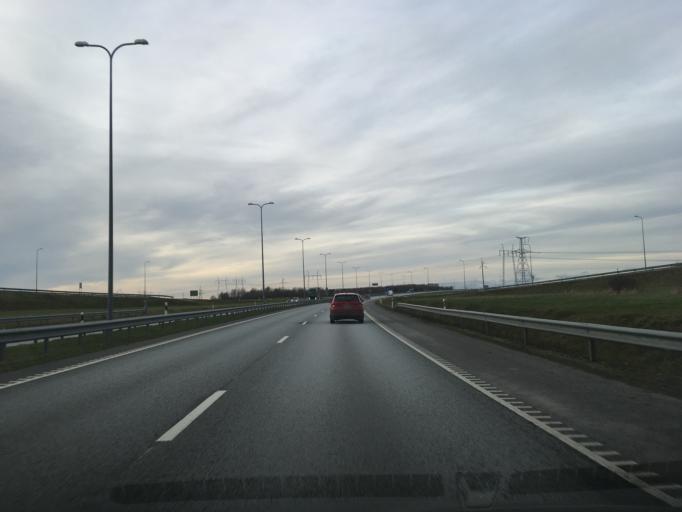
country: EE
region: Ida-Virumaa
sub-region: Kohtla-Jaerve linn
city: Kohtla-Jarve
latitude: 59.3865
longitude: 27.3476
